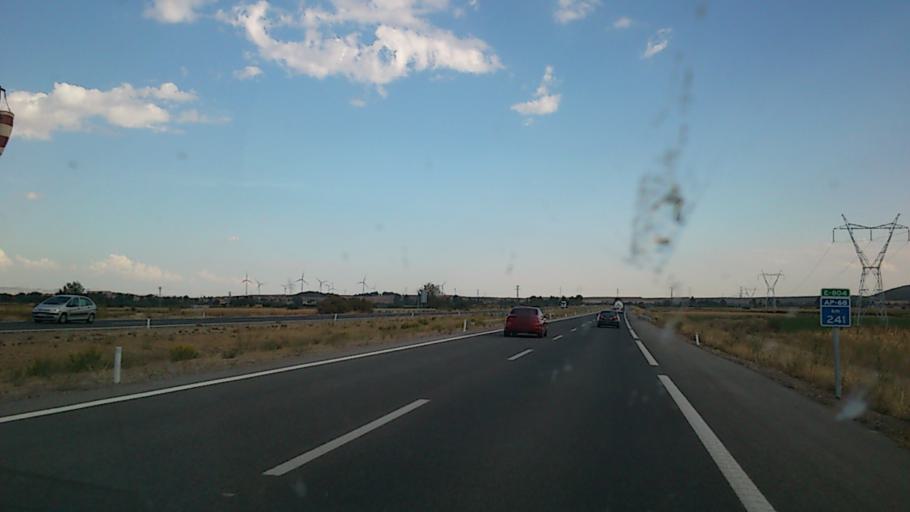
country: ES
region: Aragon
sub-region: Provincia de Zaragoza
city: Frescano
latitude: 41.9038
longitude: -1.4483
